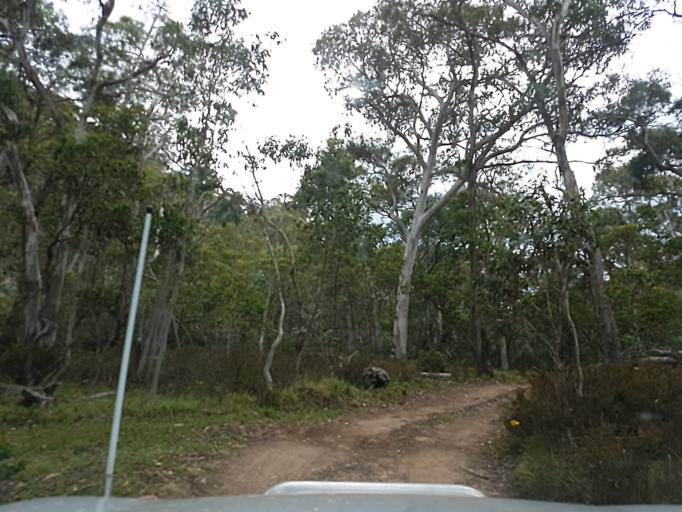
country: AU
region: New South Wales
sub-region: Snowy River
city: Jindabyne
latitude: -36.8882
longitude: 148.1248
